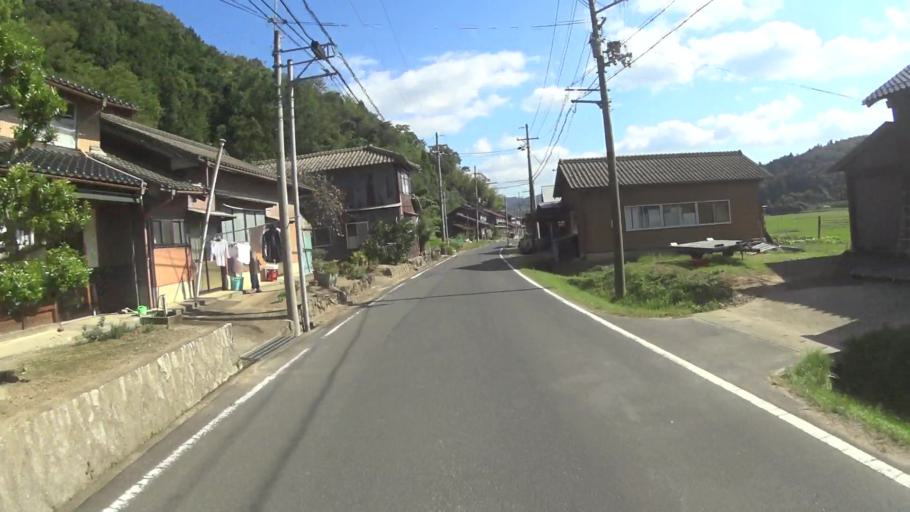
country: JP
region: Kyoto
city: Miyazu
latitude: 35.7076
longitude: 135.0936
